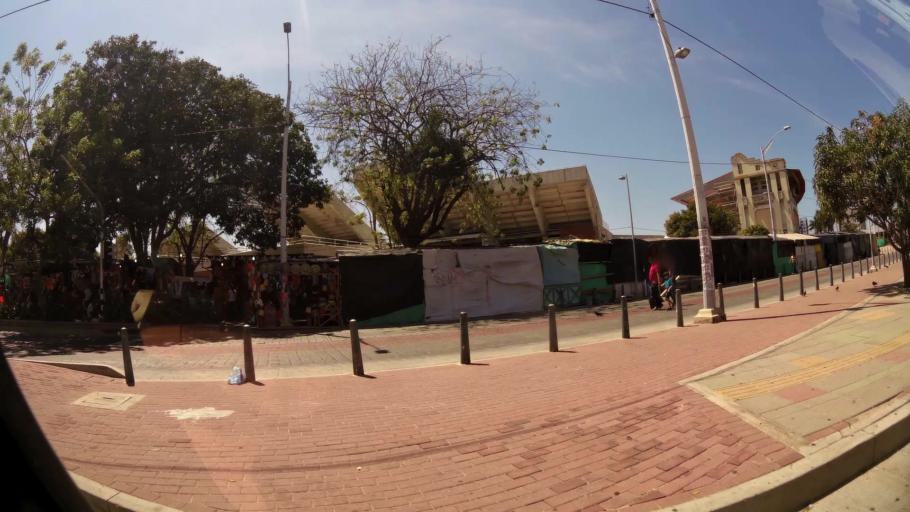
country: CO
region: Atlantico
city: Barranquilla
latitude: 10.9946
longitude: -74.8059
